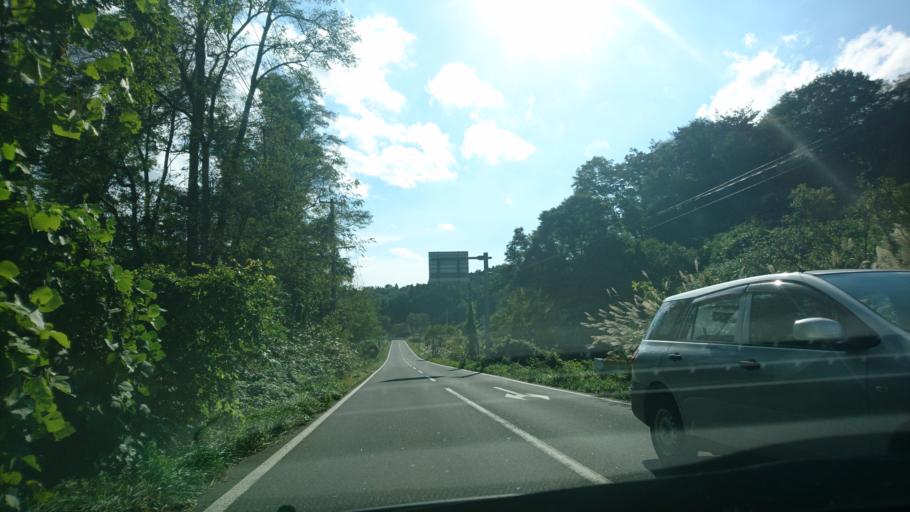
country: JP
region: Iwate
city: Ichinoseki
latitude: 38.8773
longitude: 141.1182
